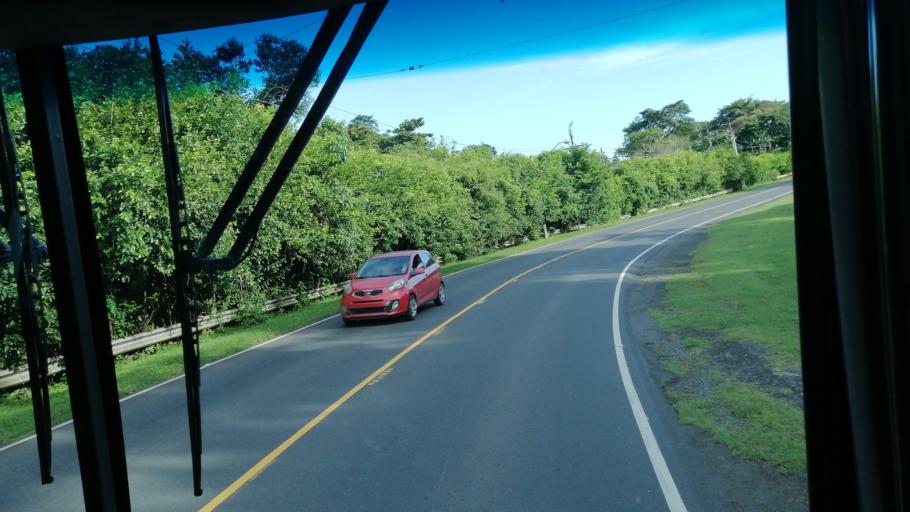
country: PA
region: Panama
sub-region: Distrito de Panama
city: Ancon
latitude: 8.9427
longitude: -79.5912
